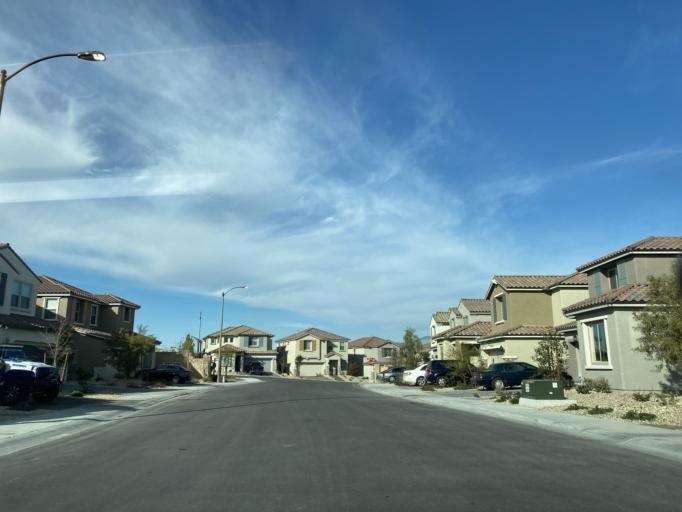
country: US
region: Nevada
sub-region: Clark County
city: Summerlin South
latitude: 36.3089
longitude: -115.3261
